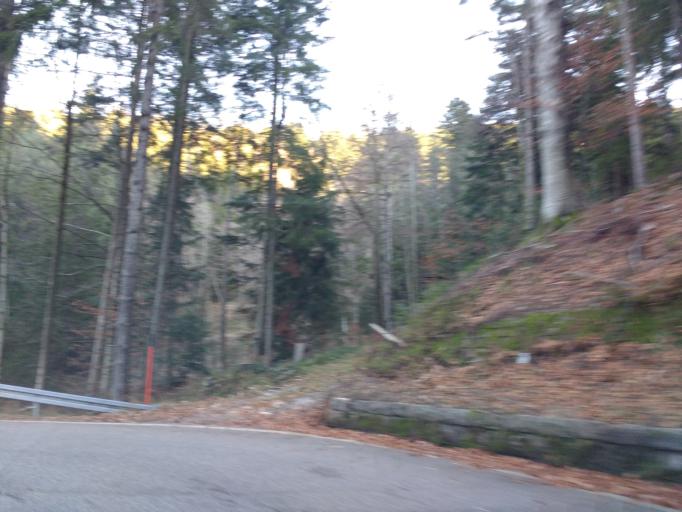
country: DE
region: Baden-Wuerttemberg
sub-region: Freiburg Region
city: Bad Peterstal-Griesbach
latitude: 48.4521
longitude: 8.2564
